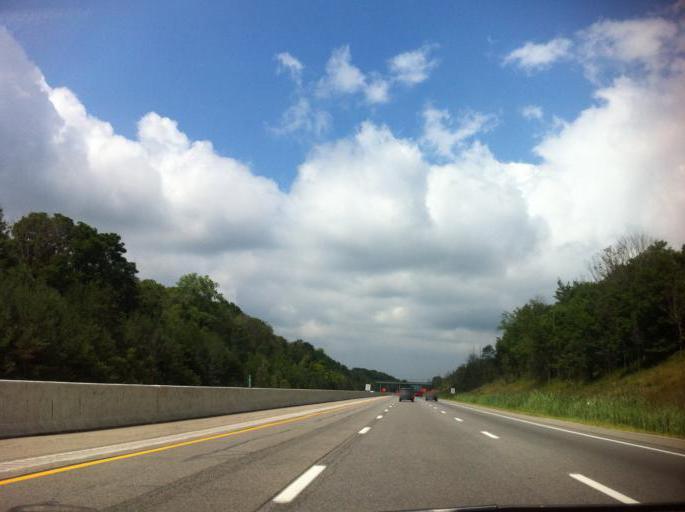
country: US
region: Ohio
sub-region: Cuyahoga County
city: North Royalton
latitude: 41.3033
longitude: -81.7247
